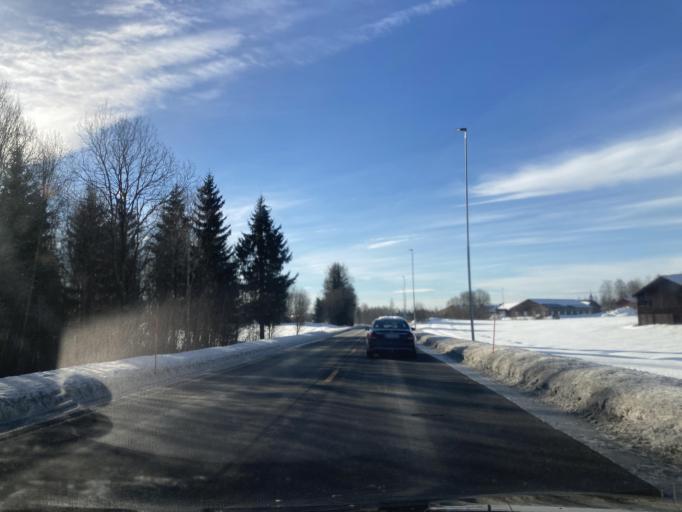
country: NO
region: Hedmark
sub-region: Elverum
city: Elverum
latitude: 60.9283
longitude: 11.6703
